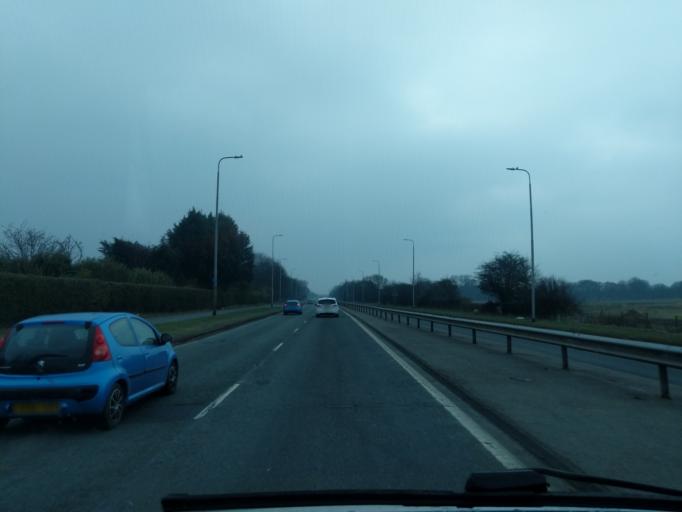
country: GB
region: England
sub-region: St. Helens
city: Haydock
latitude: 53.4725
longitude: -2.6740
